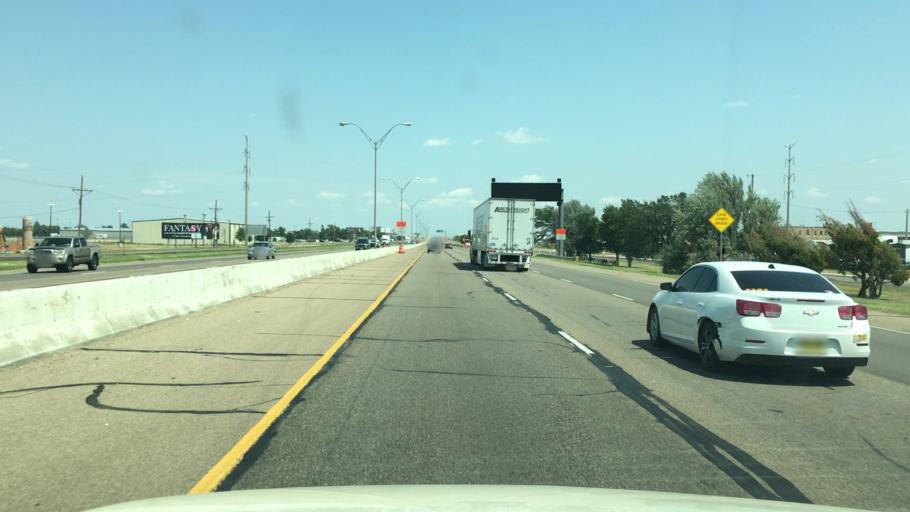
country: US
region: Texas
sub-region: Potter County
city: Amarillo
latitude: 35.1927
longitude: -101.7721
